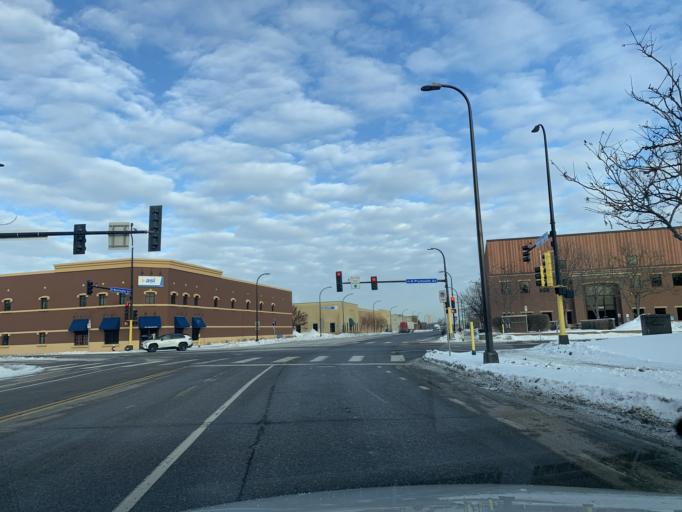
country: US
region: Minnesota
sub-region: Hennepin County
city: Minneapolis
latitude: 44.9917
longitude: -93.2813
